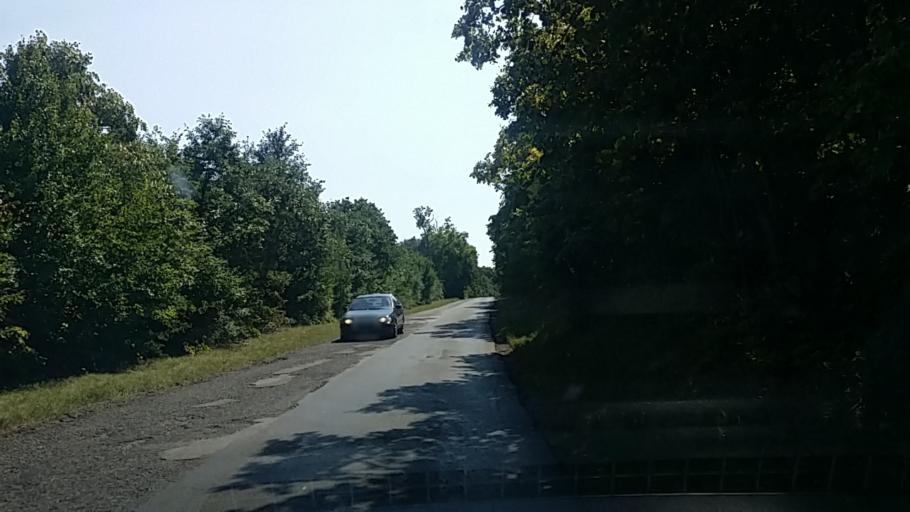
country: HU
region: Baranya
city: Pecs
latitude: 46.1177
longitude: 18.1994
